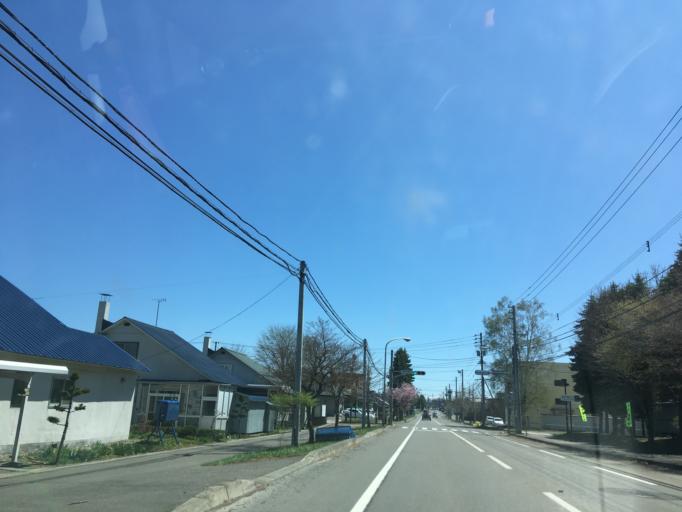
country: JP
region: Hokkaido
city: Obihiro
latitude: 42.9223
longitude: 143.1712
